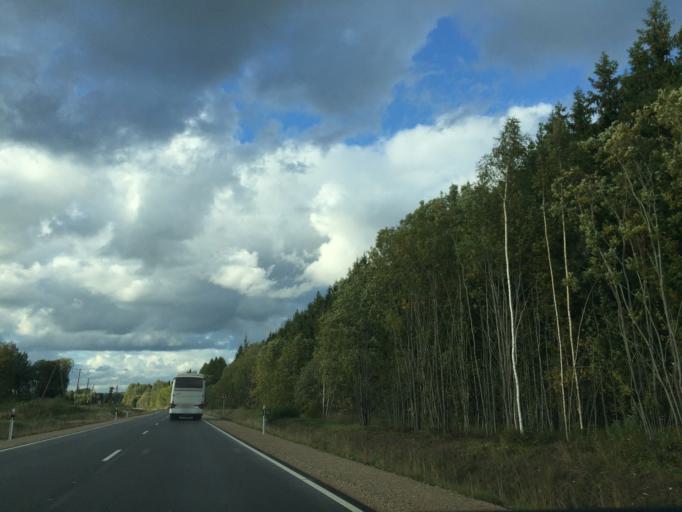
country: LV
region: Ligatne
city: Ligatne
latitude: 57.1421
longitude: 25.0798
